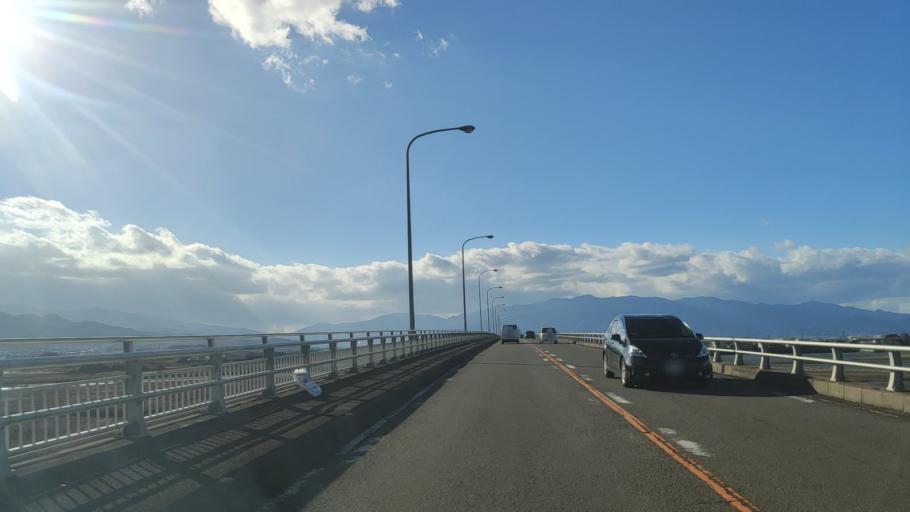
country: JP
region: Ehime
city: Saijo
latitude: 33.9183
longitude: 133.1557
